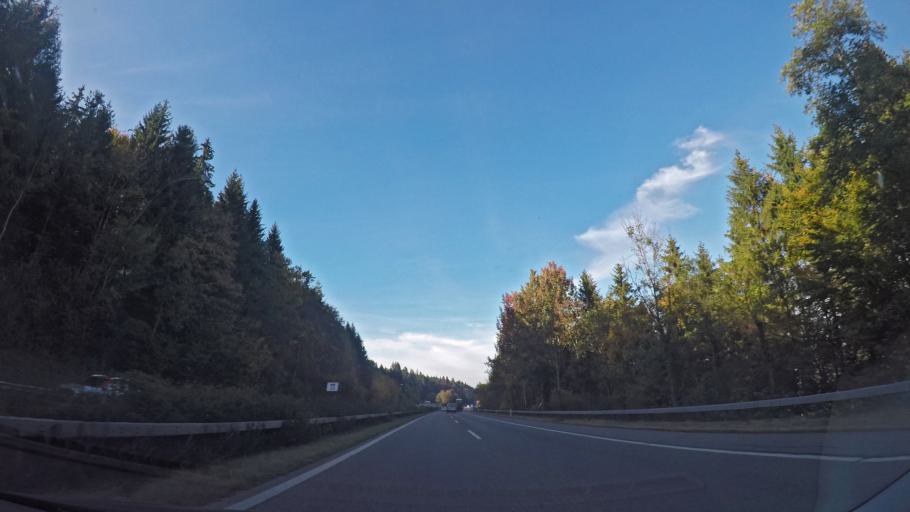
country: CH
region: Bern
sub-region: Thun District
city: Thun
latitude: 46.7290
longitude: 7.6039
